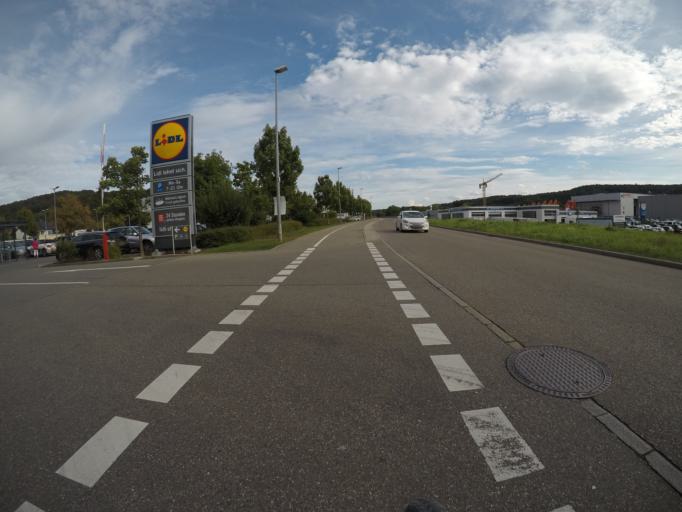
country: DE
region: Baden-Wuerttemberg
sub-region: Regierungsbezirk Stuttgart
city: Leonberg
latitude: 48.7845
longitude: 9.0197
